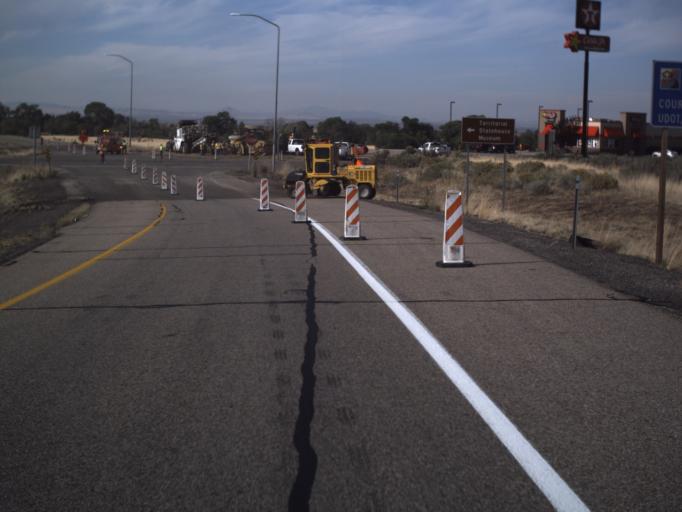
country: US
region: Utah
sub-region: Millard County
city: Fillmore
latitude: 38.9939
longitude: -112.3231
